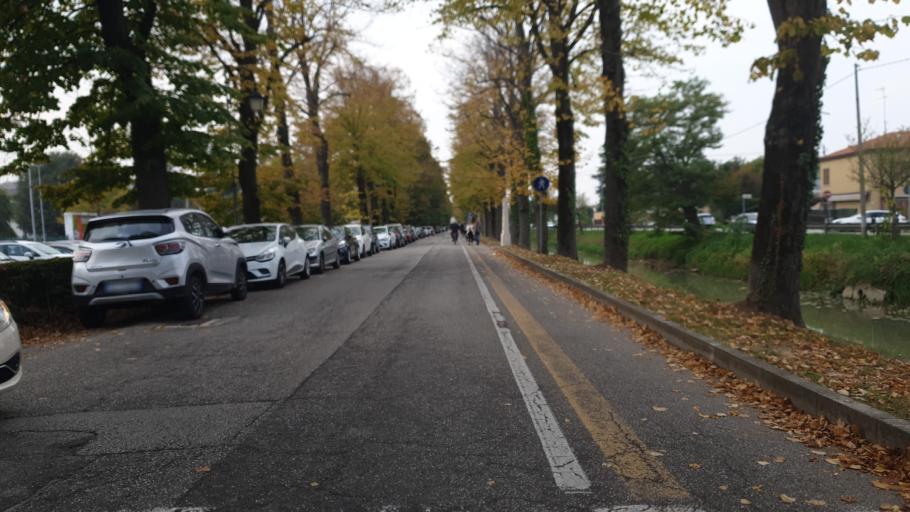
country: IT
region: Veneto
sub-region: Provincia di Padova
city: Piove di Sacco-Piovega
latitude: 45.2984
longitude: 12.0292
